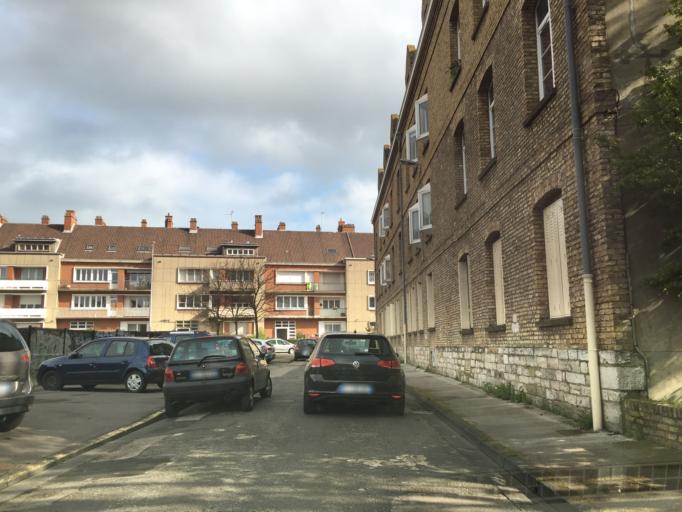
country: FR
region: Nord-Pas-de-Calais
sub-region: Departement du Nord
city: Dunkerque
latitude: 51.0368
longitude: 2.3829
